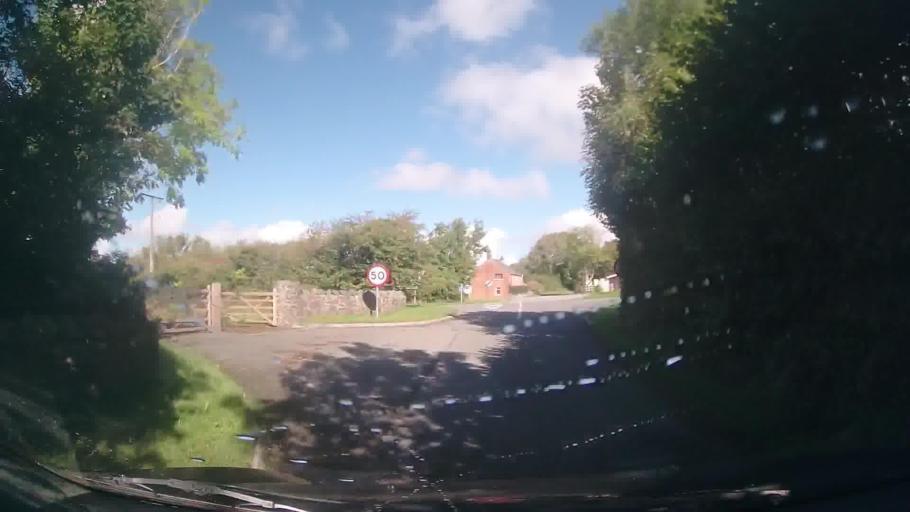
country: GB
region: Wales
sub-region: Pembrokeshire
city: Saundersfoot
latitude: 51.7573
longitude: -4.6521
